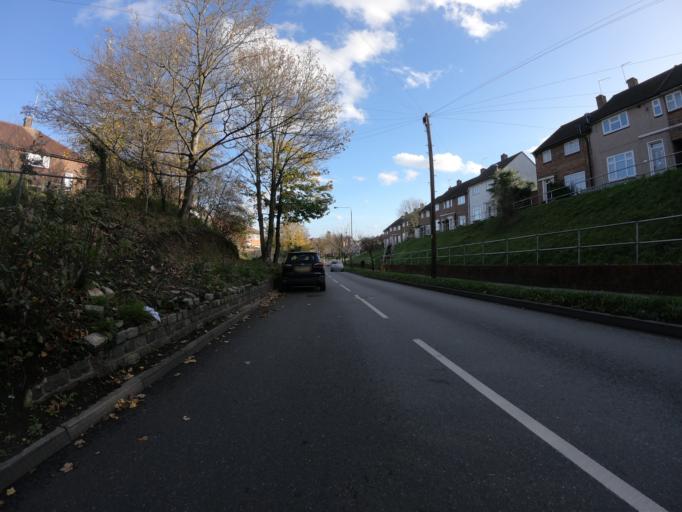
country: GB
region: England
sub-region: Greater London
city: Orpington
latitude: 51.3977
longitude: 0.1011
